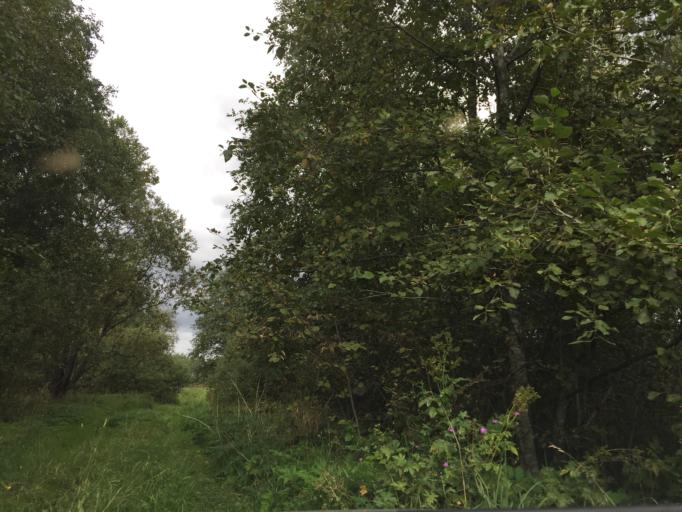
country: LV
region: Pargaujas
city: Stalbe
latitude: 57.4935
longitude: 24.9138
